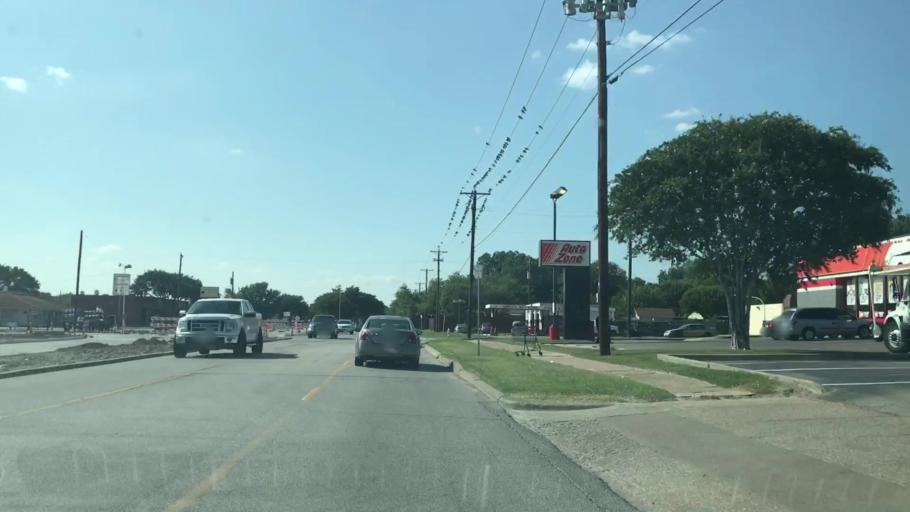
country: US
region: Texas
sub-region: Dallas County
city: Mesquite
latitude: 32.8256
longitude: -96.6484
